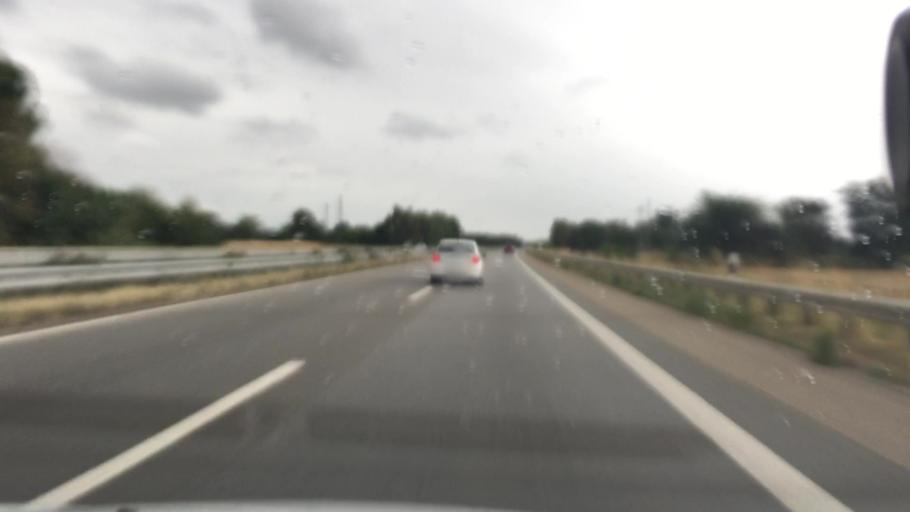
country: DE
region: Rheinland-Pfalz
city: Lachen-Speyerdorf
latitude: 49.3443
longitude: 8.1909
